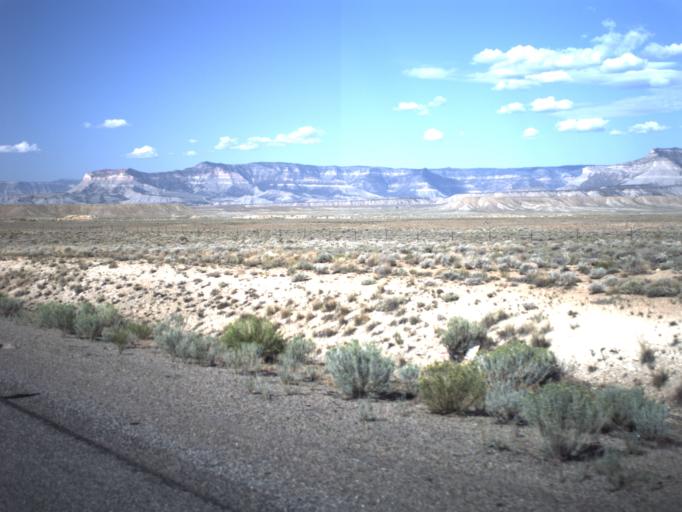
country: US
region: Utah
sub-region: Emery County
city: Huntington
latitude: 39.3942
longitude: -110.8965
